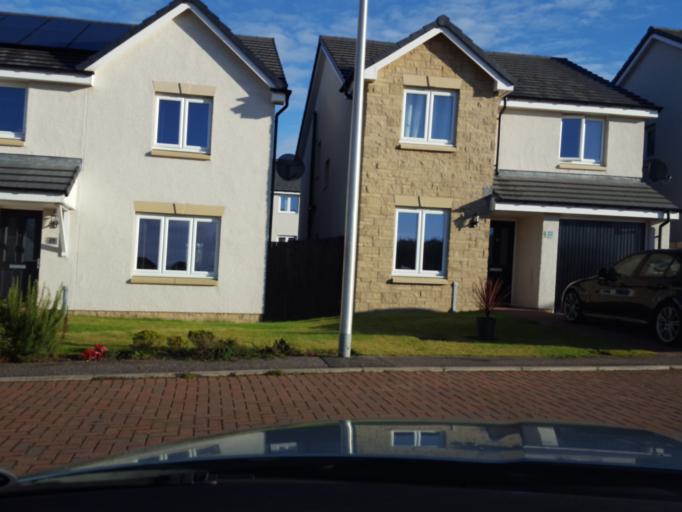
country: GB
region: Scotland
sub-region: Fife
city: Crossgates
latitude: 56.0746
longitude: -3.4071
